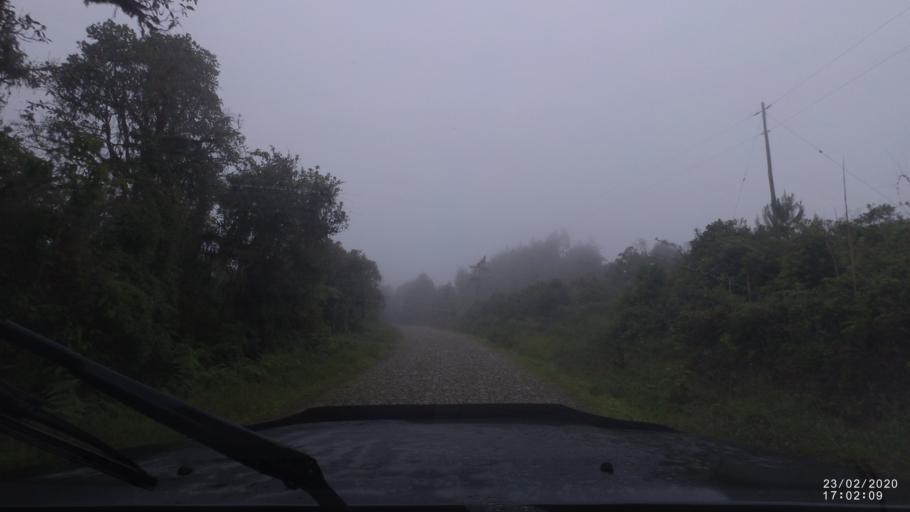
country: BO
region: Cochabamba
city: Colomi
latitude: -17.1149
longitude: -65.9635
